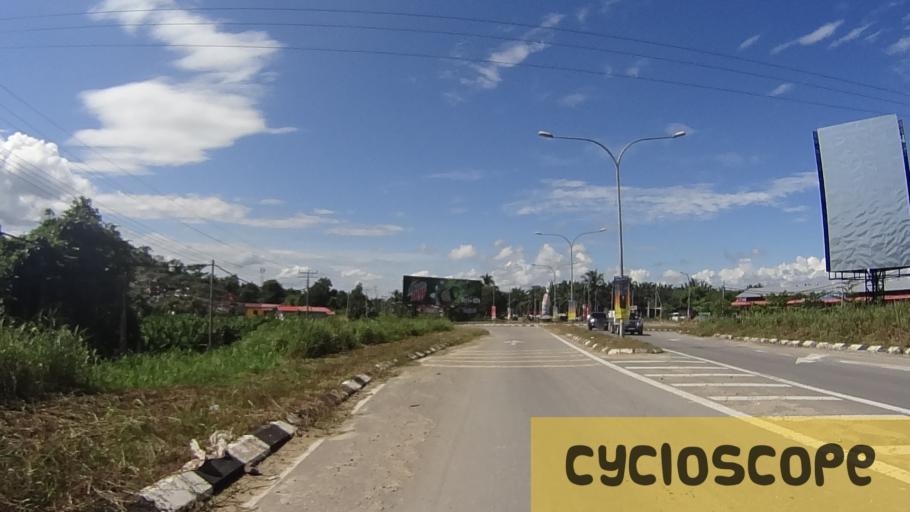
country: MY
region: Sabah
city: Beaufort
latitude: 5.3419
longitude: 115.7259
